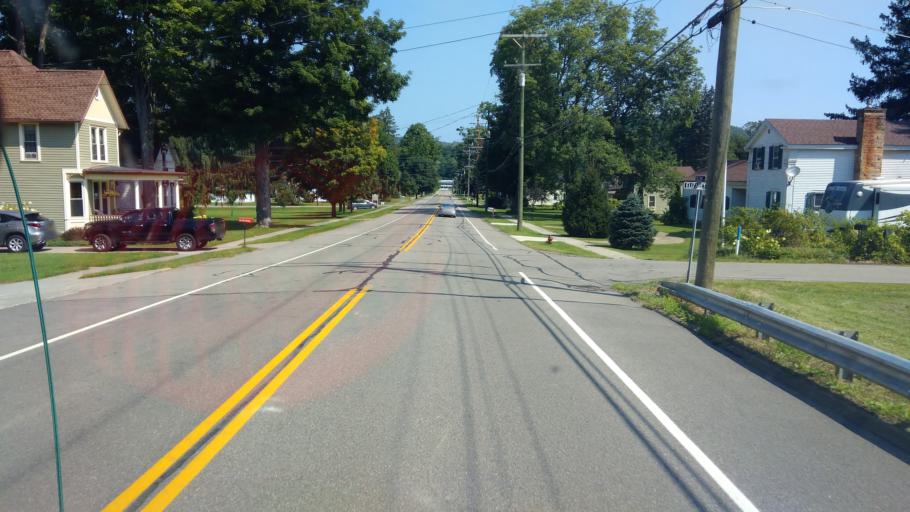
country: US
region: New York
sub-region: Allegany County
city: Belmont
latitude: 42.3024
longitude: -78.0252
